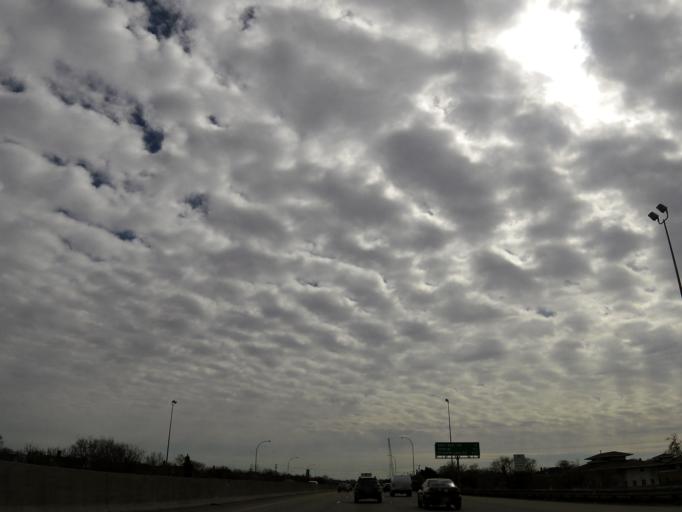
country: US
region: Minnesota
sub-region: Hennepin County
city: Minneapolis
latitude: 44.9478
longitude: -93.2749
